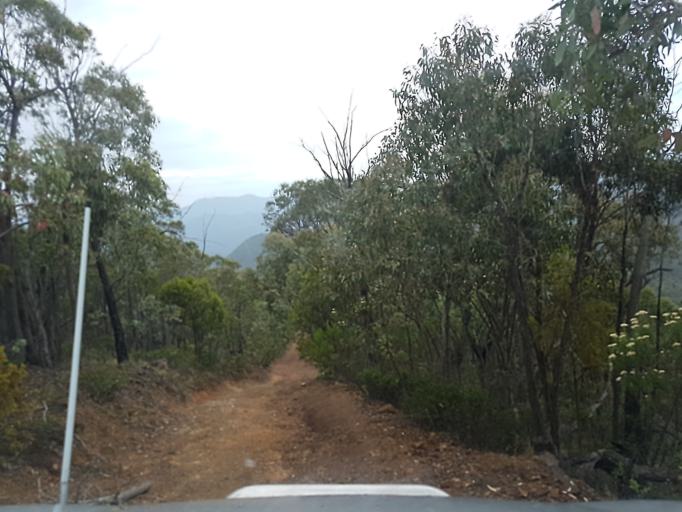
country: AU
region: New South Wales
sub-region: Snowy River
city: Jindabyne
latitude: -36.9247
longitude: 148.3529
